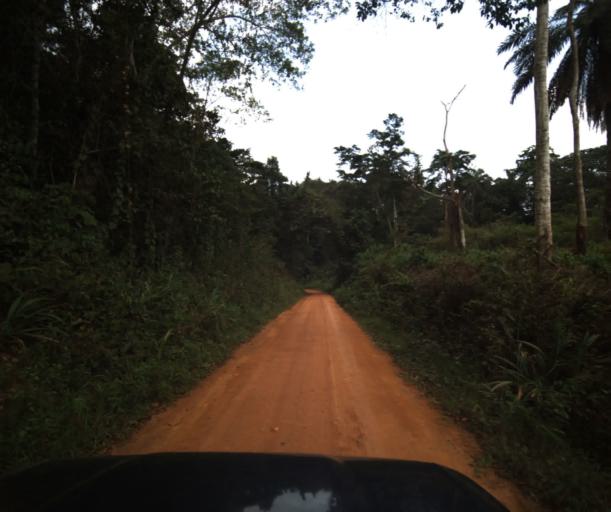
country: CM
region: Centre
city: Akono
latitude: 3.5948
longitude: 11.1653
